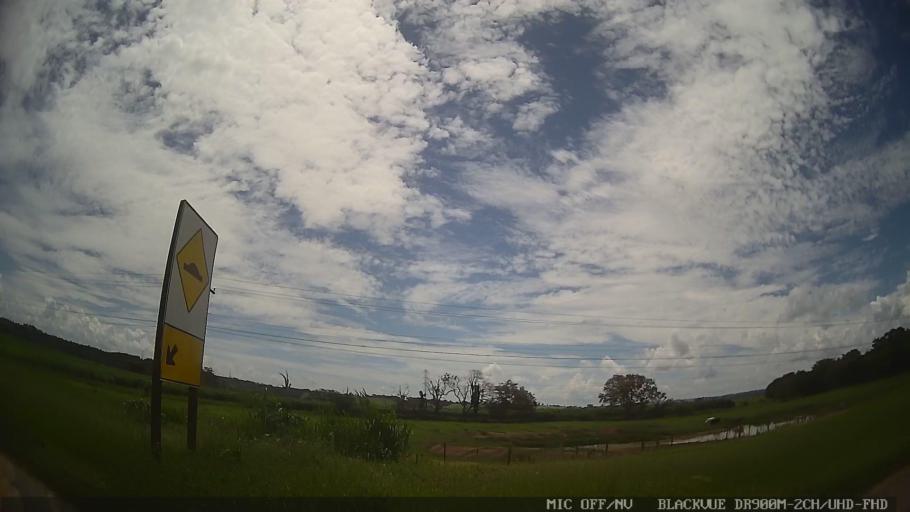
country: BR
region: Sao Paulo
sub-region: Conchas
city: Conchas
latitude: -23.0624
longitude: -47.9692
